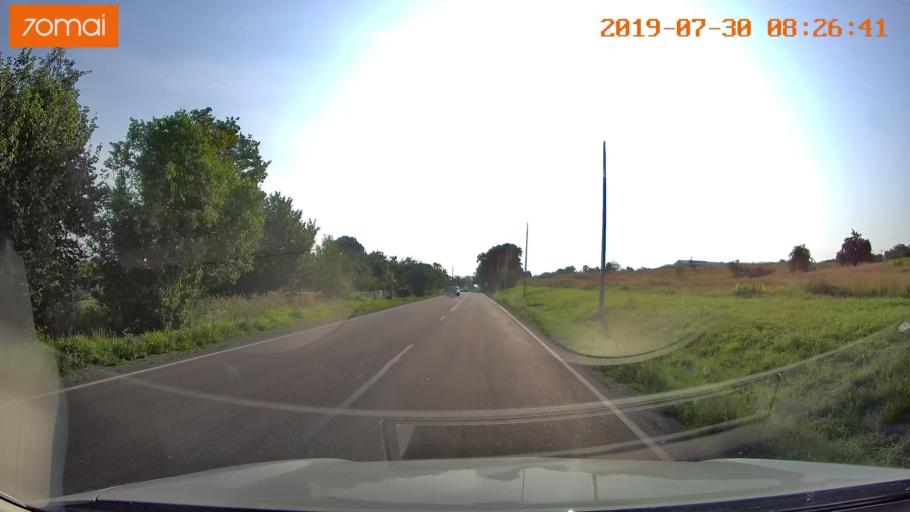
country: RU
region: Kaliningrad
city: Chernyakhovsk
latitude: 54.6258
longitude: 21.6107
